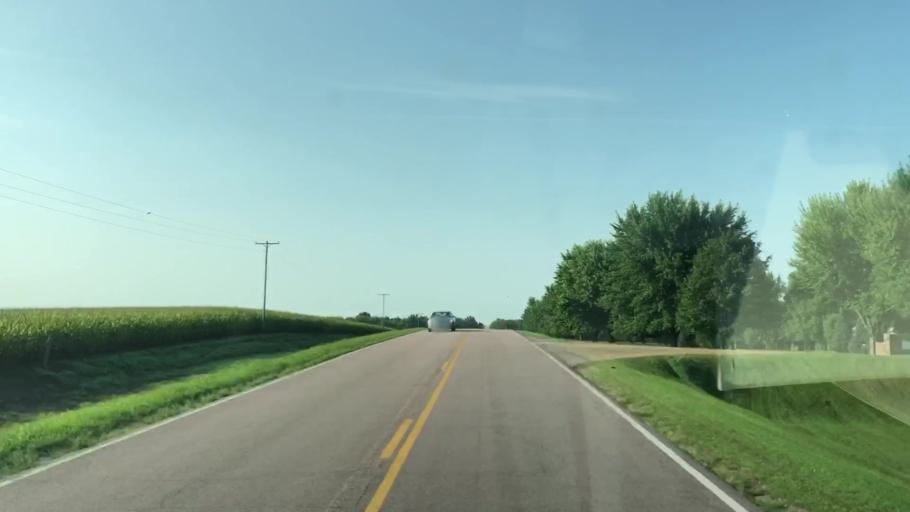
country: US
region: Iowa
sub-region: Lyon County
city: George
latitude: 43.2620
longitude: -96.0001
